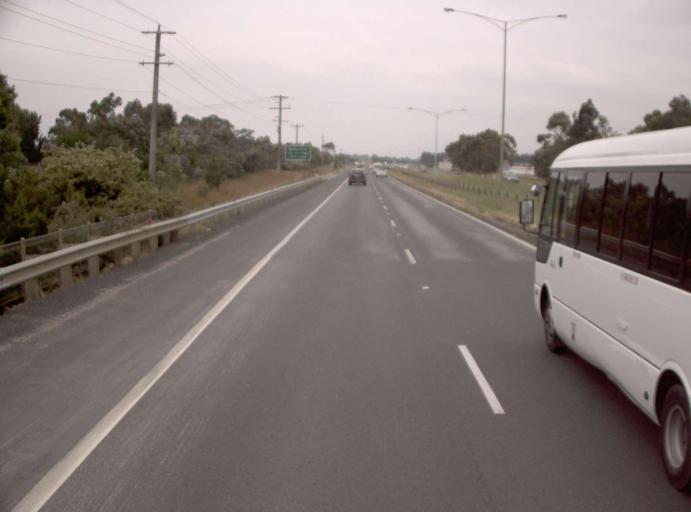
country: AU
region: Victoria
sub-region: Latrobe
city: Traralgon
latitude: -38.2210
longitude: 146.4717
